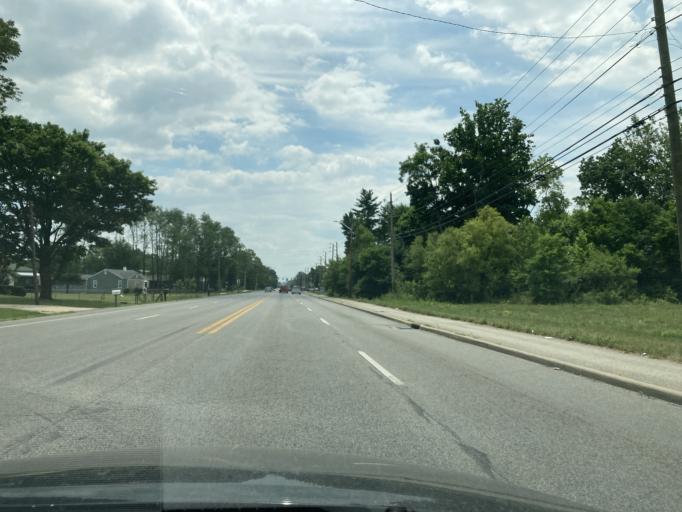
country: US
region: Indiana
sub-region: Marion County
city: Meridian Hills
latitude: 39.8704
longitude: -86.2029
